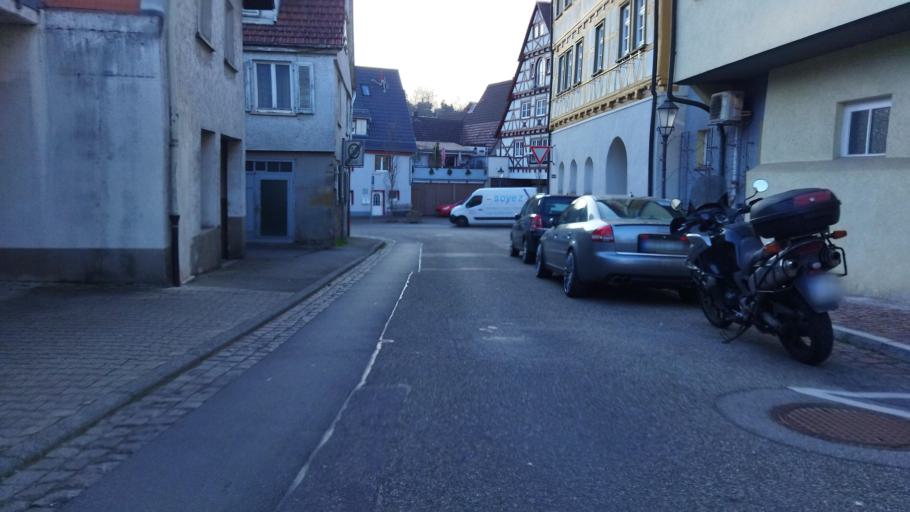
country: DE
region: Baden-Wuerttemberg
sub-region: Regierungsbezirk Stuttgart
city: Gemmrigheim
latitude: 49.0254
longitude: 9.1559
